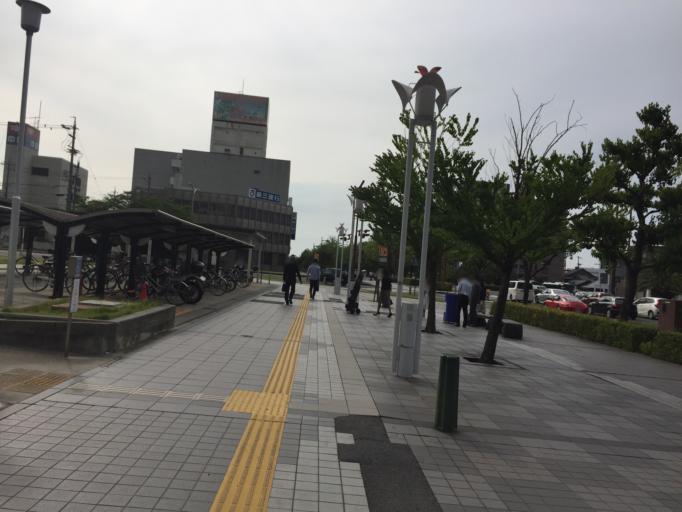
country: JP
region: Mie
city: Yokkaichi
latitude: 34.9647
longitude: 136.6245
